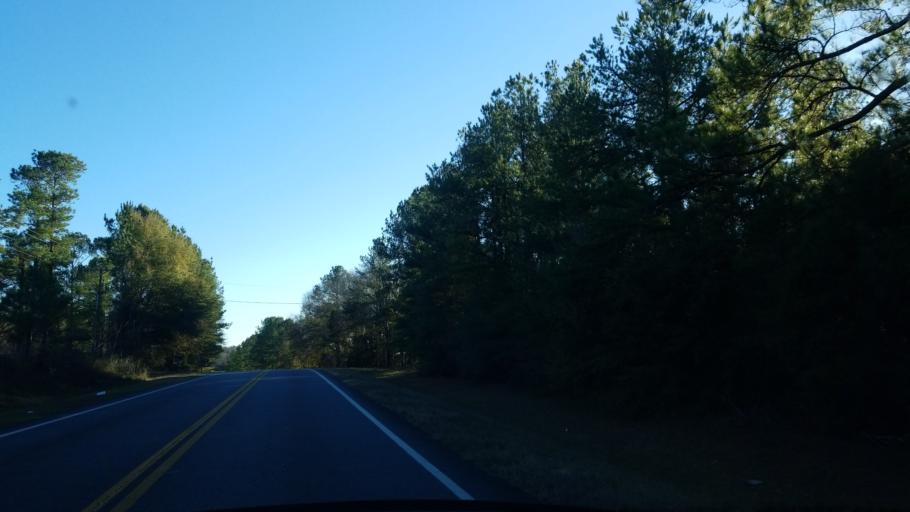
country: US
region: Georgia
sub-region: Talbot County
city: Talbotton
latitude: 32.5553
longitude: -84.6043
